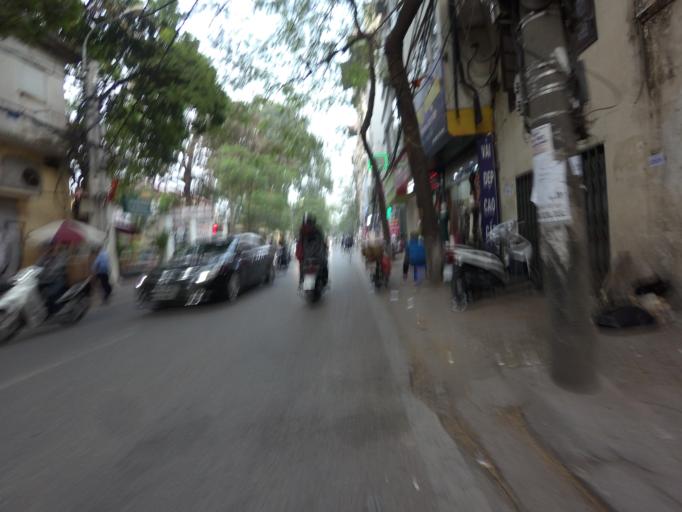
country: VN
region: Ha Noi
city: Hanoi
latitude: 21.0428
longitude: 105.8338
